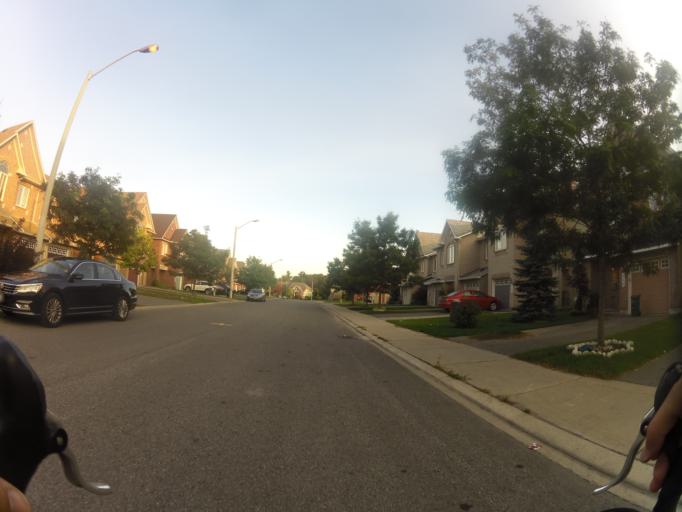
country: CA
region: Ontario
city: Bells Corners
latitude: 45.3450
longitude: -75.9424
